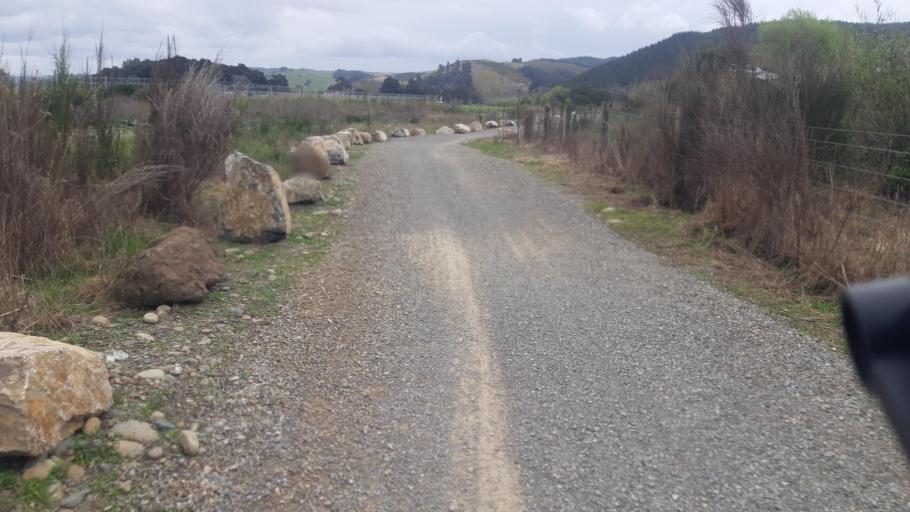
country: NZ
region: Tasman
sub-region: Tasman District
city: Wakefield
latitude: -41.4049
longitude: 173.0280
